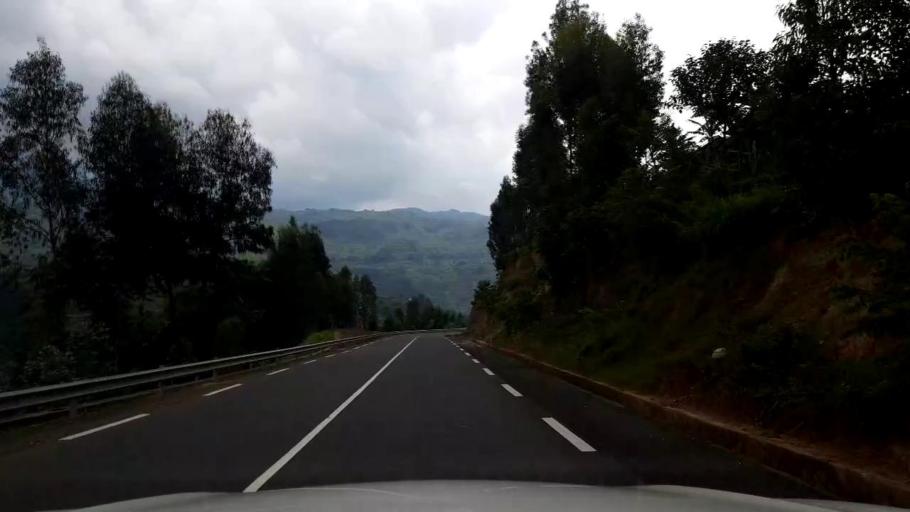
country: RW
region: Western Province
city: Kibuye
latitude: -1.9052
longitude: 29.3649
